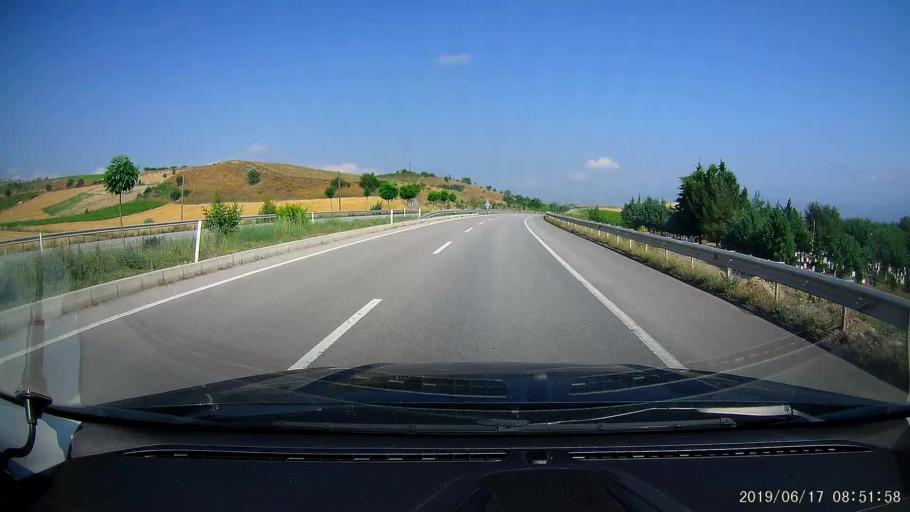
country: TR
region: Tokat
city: Erbaa
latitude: 40.6920
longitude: 36.5049
